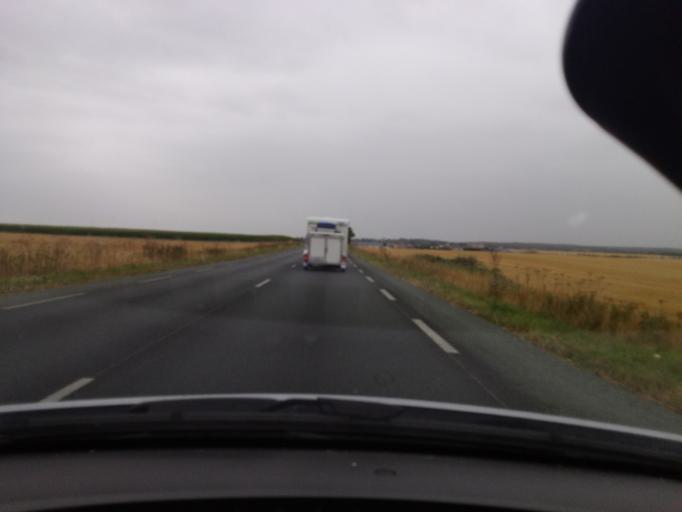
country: FR
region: Pays de la Loire
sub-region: Departement de la Vendee
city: Sainte-Gemme-la-Plaine
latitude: 46.4977
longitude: -1.1032
